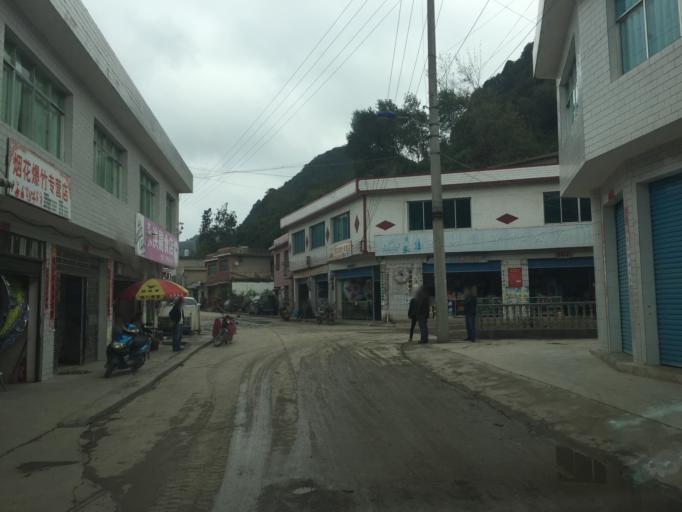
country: CN
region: Guizhou Sheng
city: Guiyang
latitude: 26.9014
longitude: 107.2155
